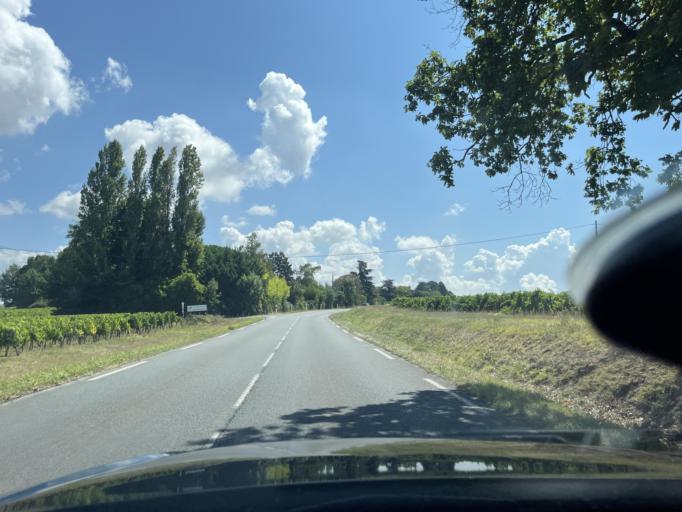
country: FR
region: Aquitaine
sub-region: Departement de la Gironde
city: Cantenac
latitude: 45.0708
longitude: -0.6255
